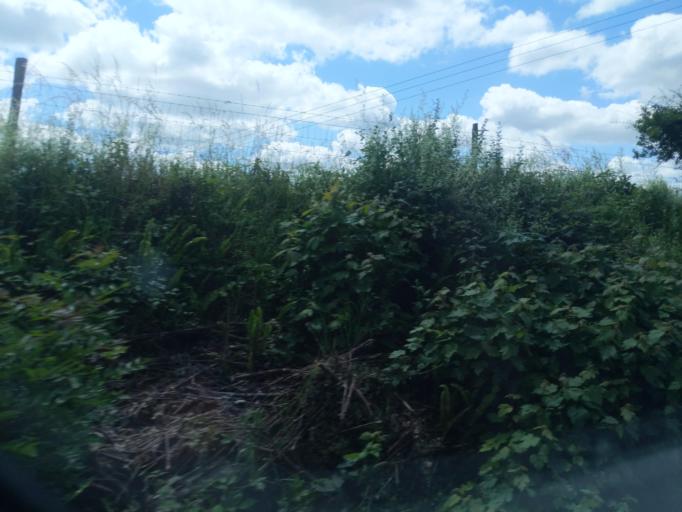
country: GB
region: England
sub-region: Cornwall
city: Liskeard
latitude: 50.4393
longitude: -4.4507
